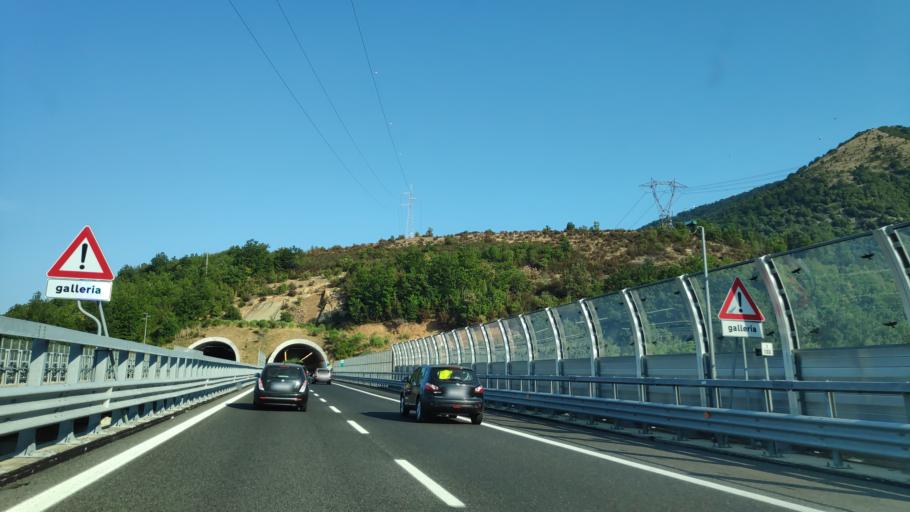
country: IT
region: Basilicate
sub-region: Provincia di Potenza
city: Lagonegro
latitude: 40.1247
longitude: 15.7800
